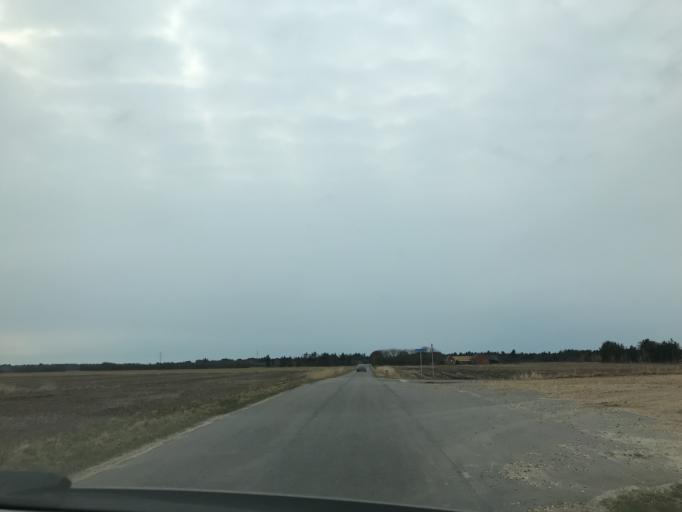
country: DK
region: South Denmark
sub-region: Varde Kommune
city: Oksbol
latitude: 55.8181
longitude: 8.2436
